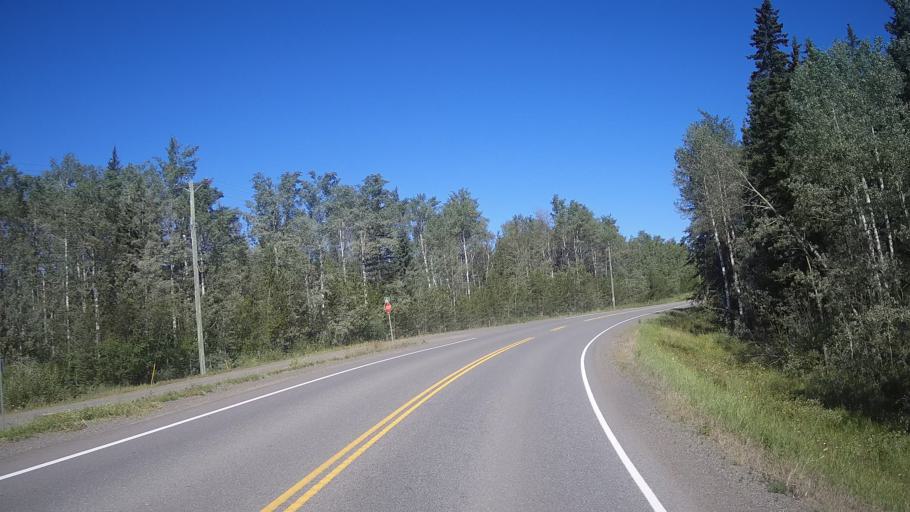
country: CA
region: British Columbia
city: Cache Creek
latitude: 51.5430
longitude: -120.9101
